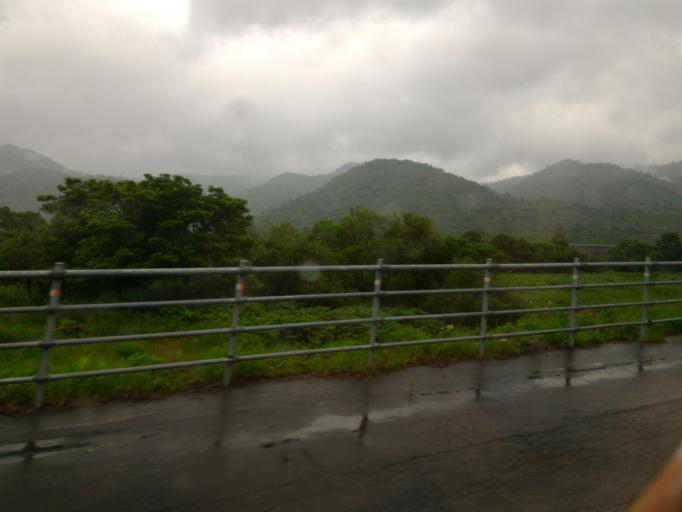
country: JP
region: Hokkaido
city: Nayoro
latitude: 44.7331
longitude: 142.1930
